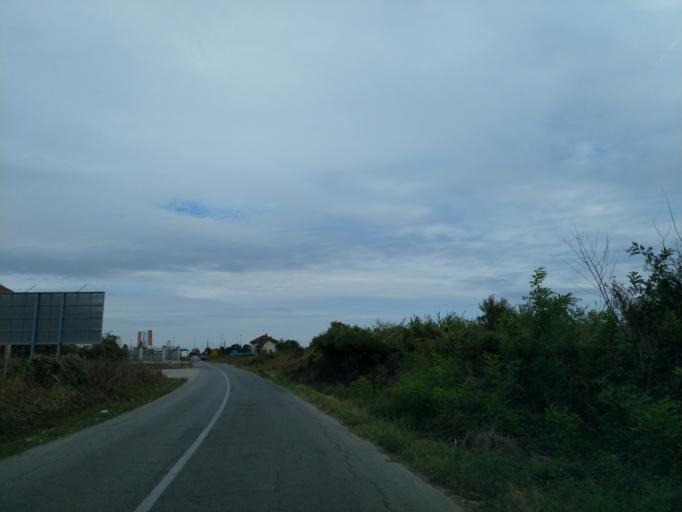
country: RS
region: Central Serbia
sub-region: Pomoravski Okrug
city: Cuprija
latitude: 43.9514
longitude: 21.3186
